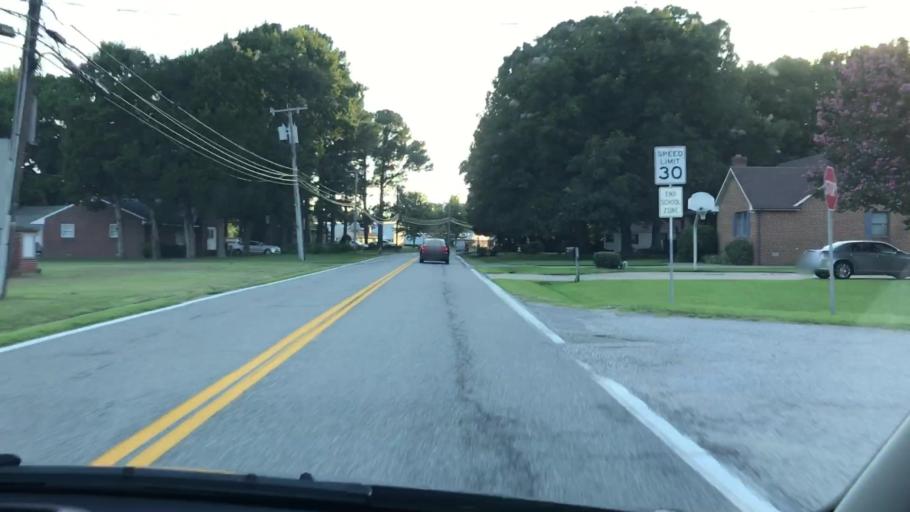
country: US
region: Virginia
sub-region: City of Hampton
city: Hampton
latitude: 37.0554
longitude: -76.3751
